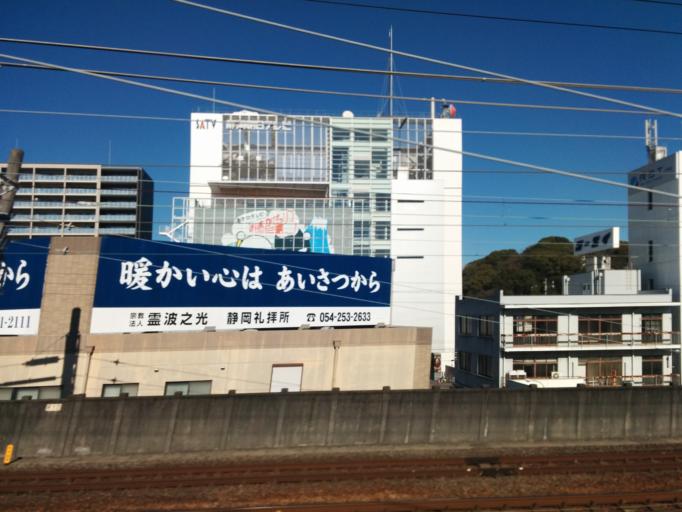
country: JP
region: Shizuoka
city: Shizuoka-shi
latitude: 34.9758
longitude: 138.3971
